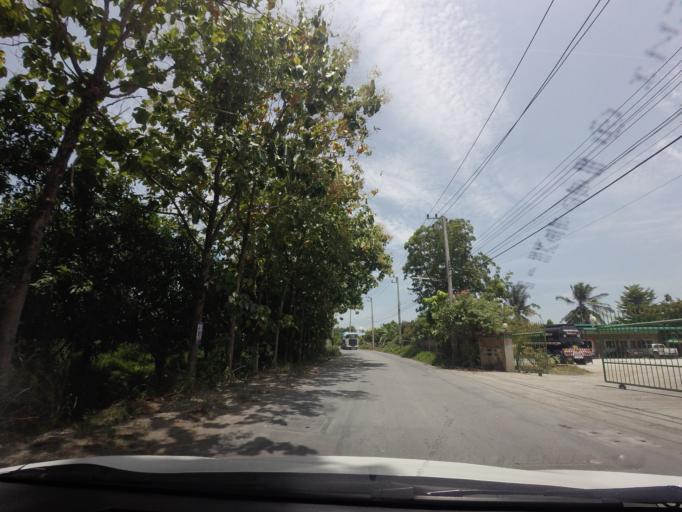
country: TH
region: Chon Buri
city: Chon Buri
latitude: 13.3032
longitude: 100.9751
